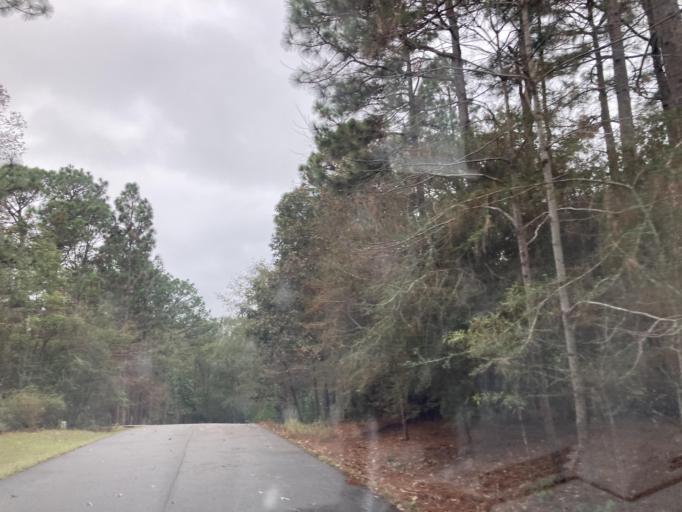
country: US
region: Mississippi
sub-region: Lamar County
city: Purvis
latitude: 31.1546
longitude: -89.4224
